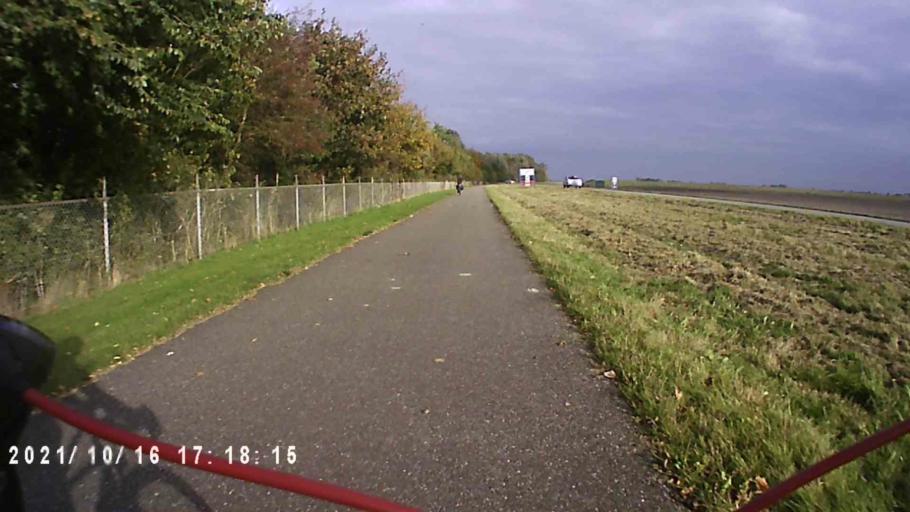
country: NL
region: Friesland
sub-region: Gemeente Kollumerland en Nieuwkruisland
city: Kollum
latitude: 53.3170
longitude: 6.1661
